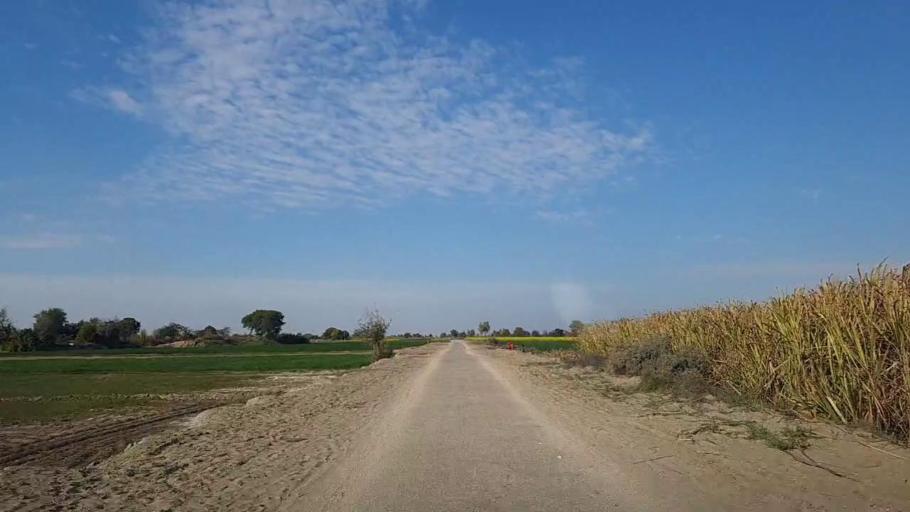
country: PK
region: Sindh
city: Khadro
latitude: 26.3043
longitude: 68.8343
